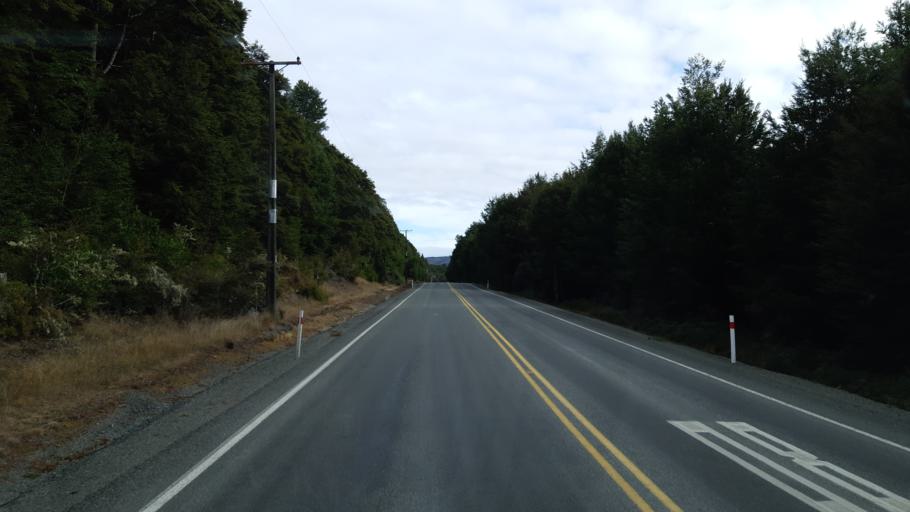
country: NZ
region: Tasman
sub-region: Tasman District
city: Wakefield
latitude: -41.7761
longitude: 172.9265
